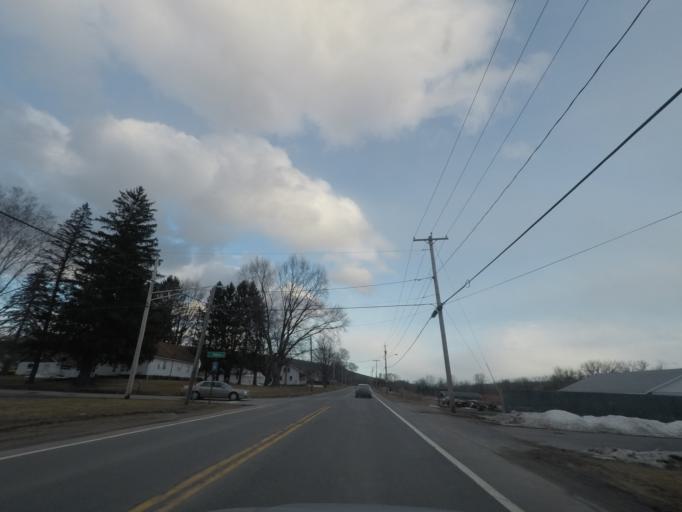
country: US
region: New York
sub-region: Herkimer County
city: Frankfort
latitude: 43.0516
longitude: -75.0708
